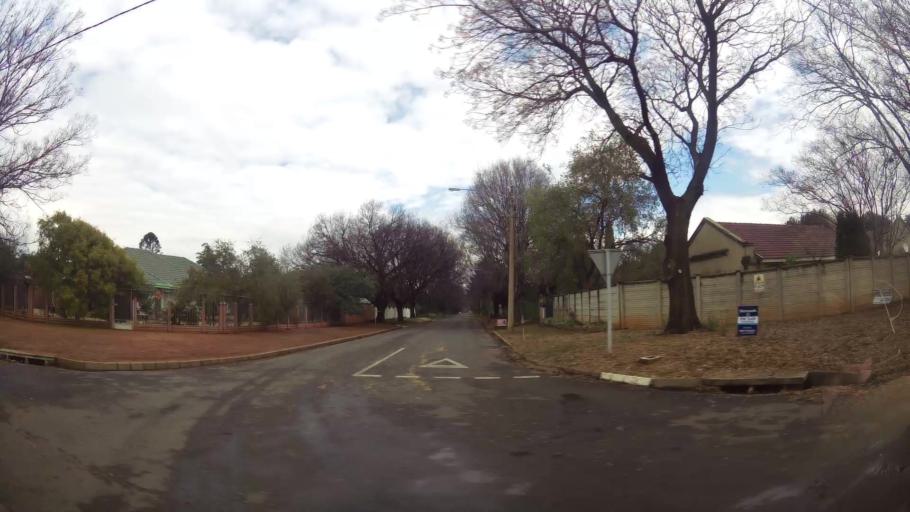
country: ZA
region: Gauteng
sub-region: Sedibeng District Municipality
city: Vereeniging
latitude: -26.6428
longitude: 27.9810
